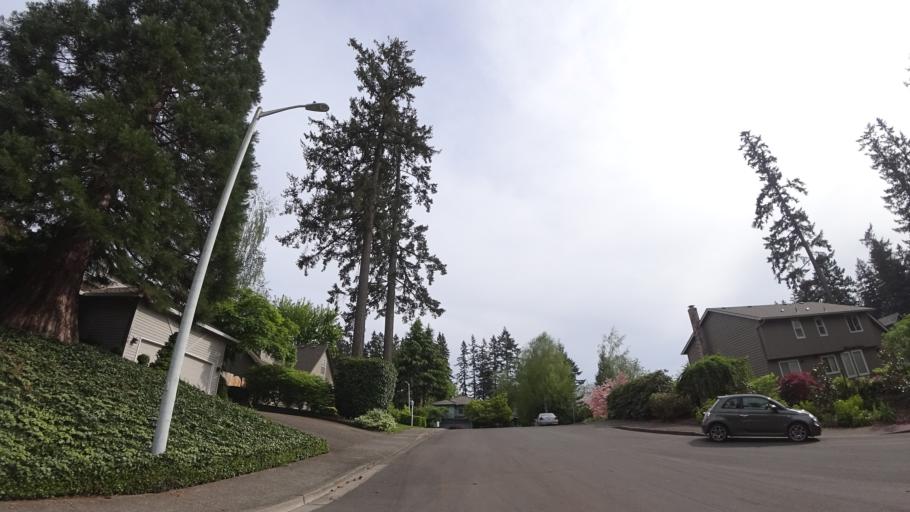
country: US
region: Oregon
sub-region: Washington County
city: Hillsboro
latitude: 45.5115
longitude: -122.9300
